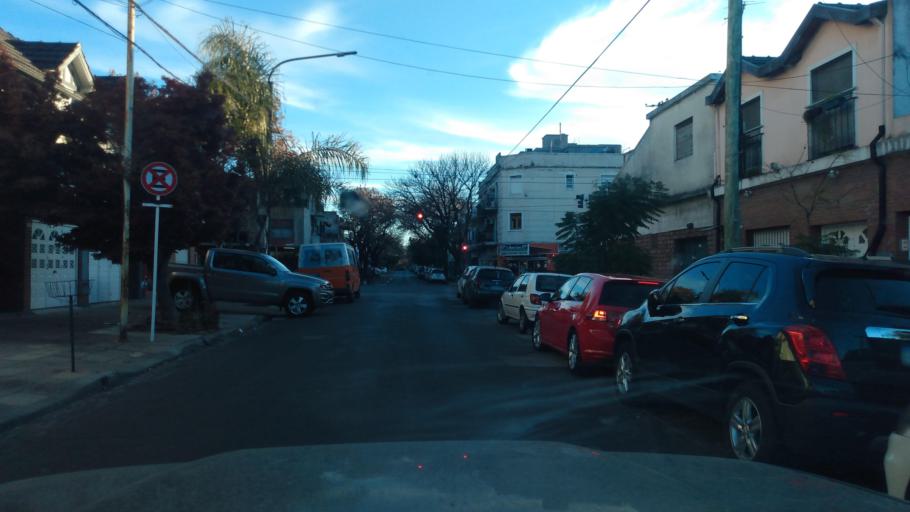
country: AR
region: Buenos Aires F.D.
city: Villa Santa Rita
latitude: -34.5853
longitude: -58.4877
